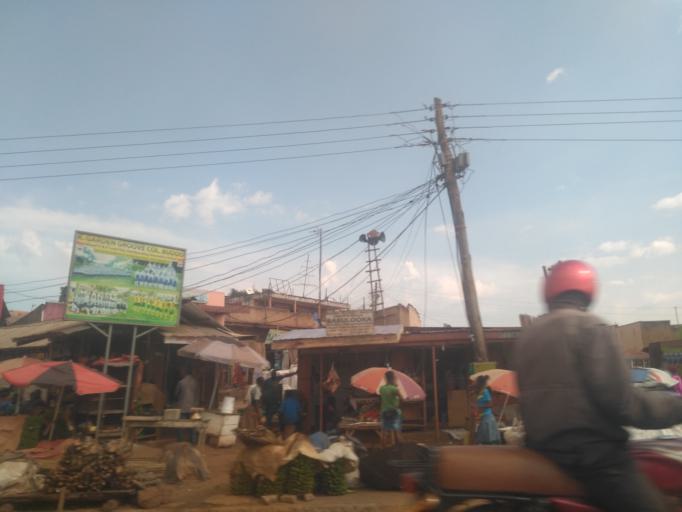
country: UG
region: Central Region
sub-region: Wakiso District
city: Kajansi
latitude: 0.2737
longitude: 32.4672
